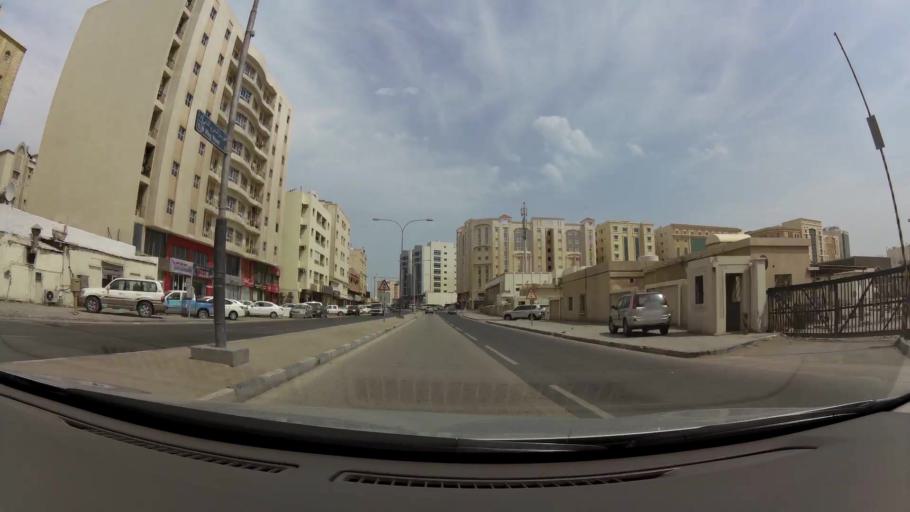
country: QA
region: Baladiyat ad Dawhah
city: Doha
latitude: 25.2750
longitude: 51.5357
